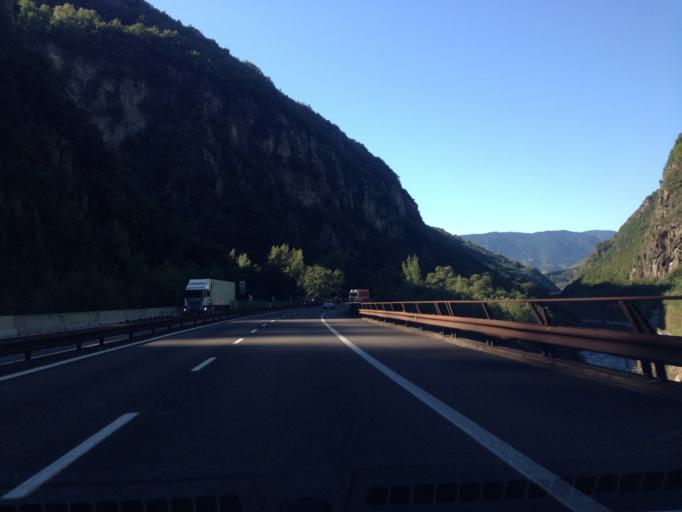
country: IT
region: Trentino-Alto Adige
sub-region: Bolzano
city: Fie Allo Sciliar
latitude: 46.5504
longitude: 11.5134
